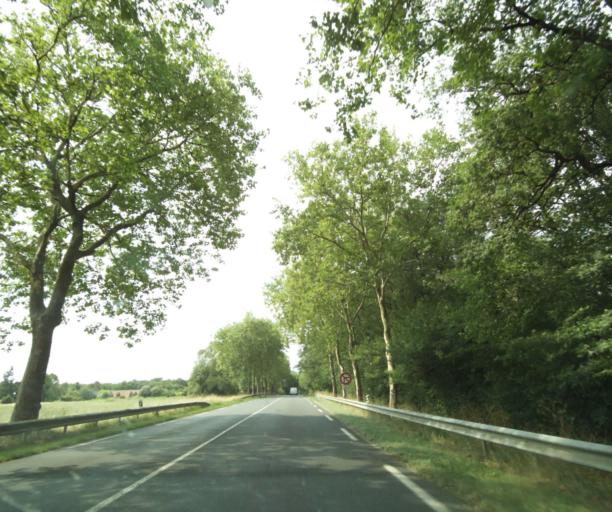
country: FR
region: Centre
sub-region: Departement d'Indre-et-Loire
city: La Membrolle-sur-Choisille
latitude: 47.4493
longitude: 0.6311
